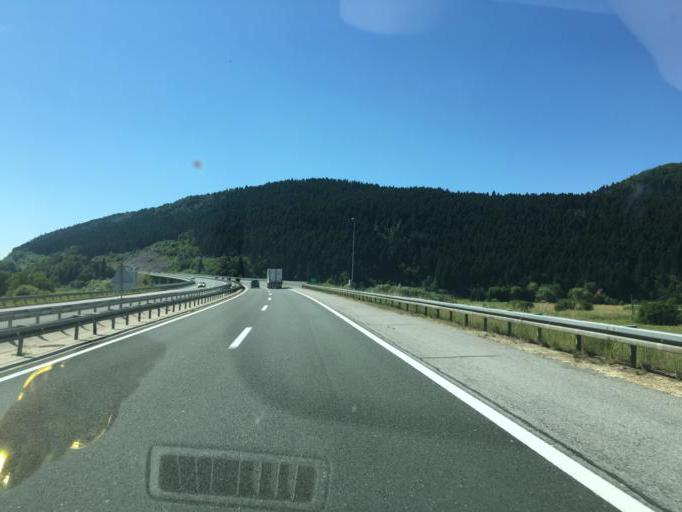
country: HR
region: Licko-Senjska
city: Otocac
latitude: 44.8652
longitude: 15.2085
